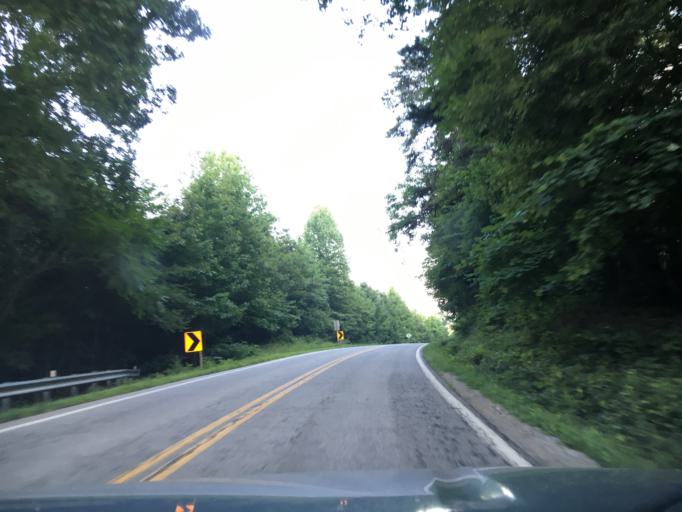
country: US
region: Virginia
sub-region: Pittsylvania County
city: Chatham
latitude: 36.8276
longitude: -79.2792
